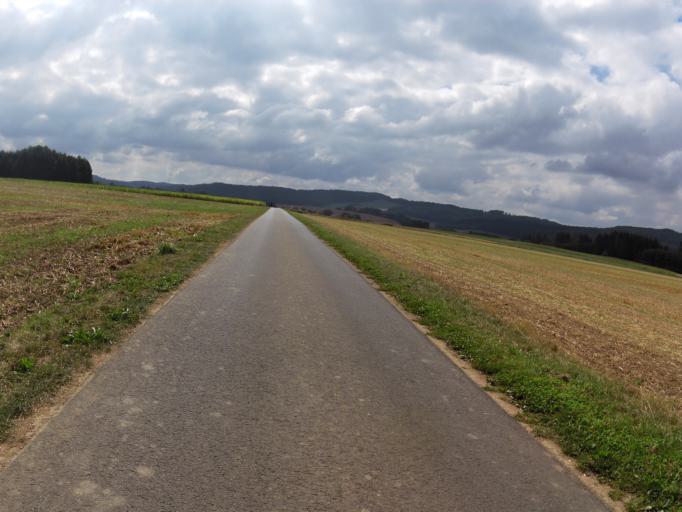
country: DE
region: Rheinland-Pfalz
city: Oberbettingen
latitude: 50.2856
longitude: 6.6469
